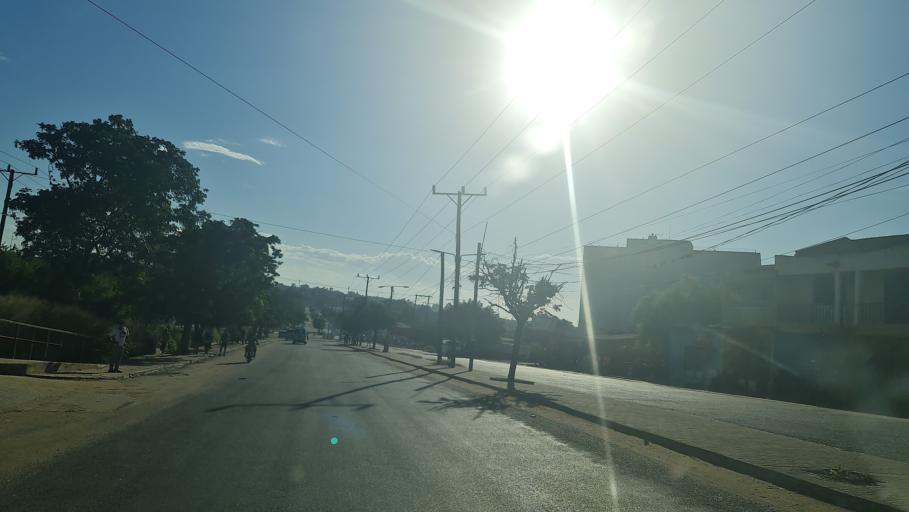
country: MZ
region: Cabo Delgado
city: Pemba
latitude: -12.9680
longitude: 40.5135
